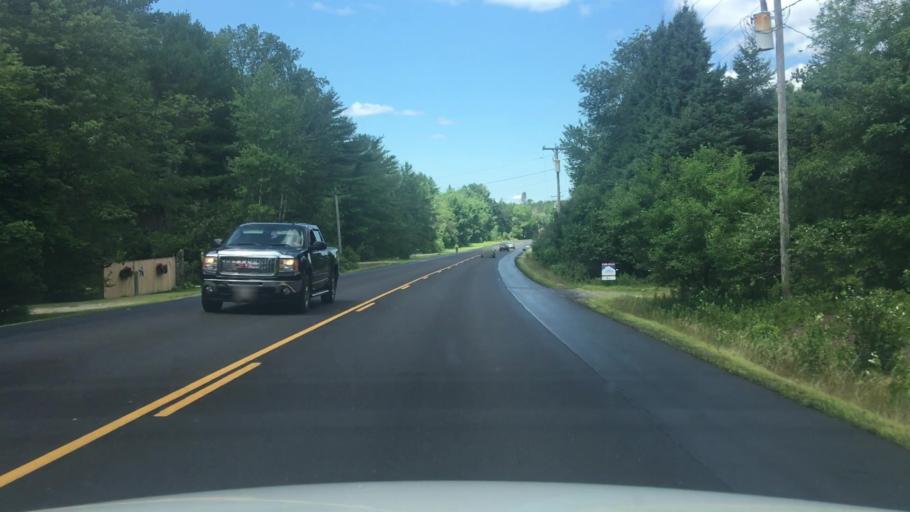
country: US
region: Maine
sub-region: Waldo County
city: Searsmont
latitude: 44.3998
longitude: -69.1577
